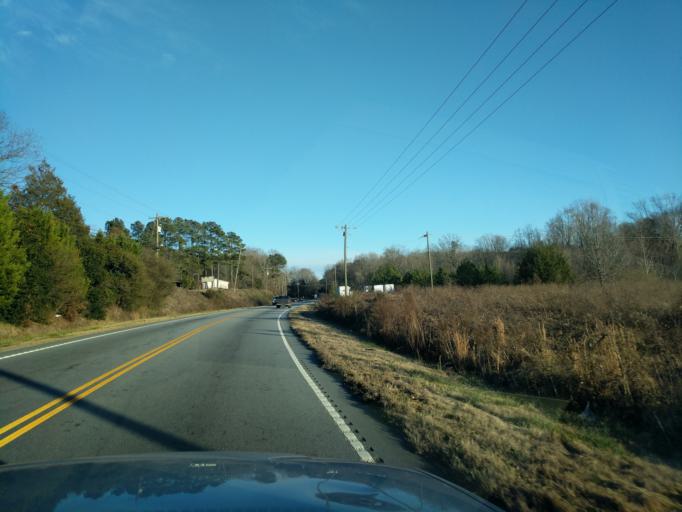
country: US
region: South Carolina
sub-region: Greenville County
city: Fountain Inn
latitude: 34.6742
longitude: -82.2309
